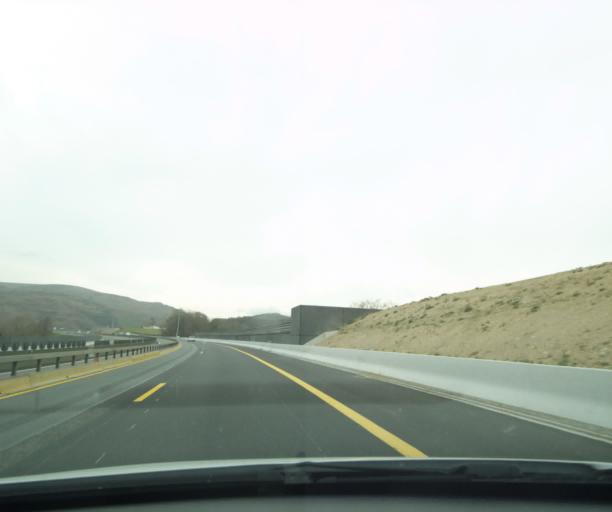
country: FR
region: Aquitaine
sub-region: Departement des Pyrenees-Atlantiques
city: Urrugne
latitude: 43.3554
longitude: -1.7170
